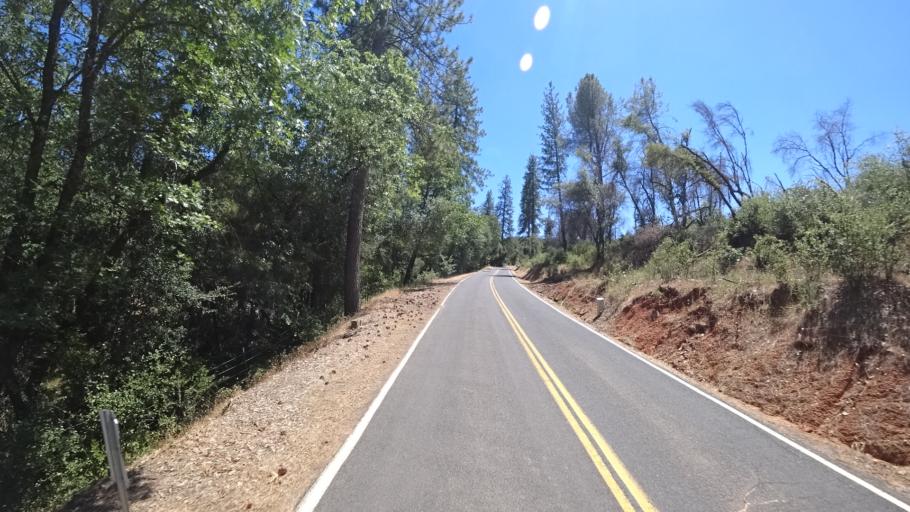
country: US
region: California
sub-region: Calaveras County
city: Forest Meadows
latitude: 38.2145
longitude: -120.4638
